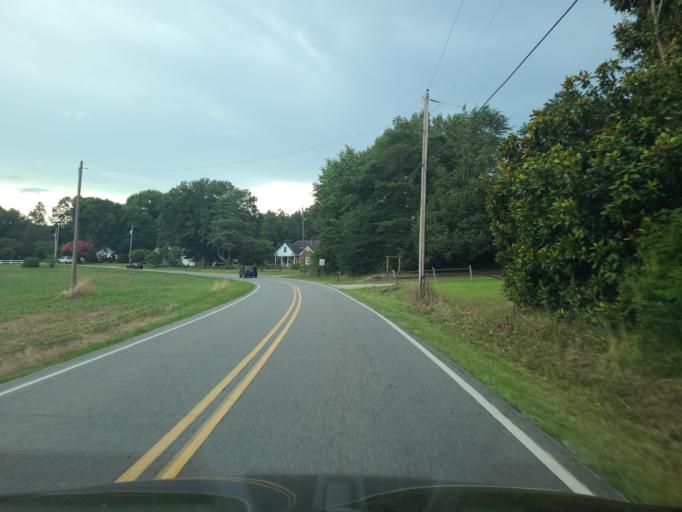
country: US
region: North Carolina
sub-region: Gaston County
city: Dallas
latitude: 35.3018
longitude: -81.1640
